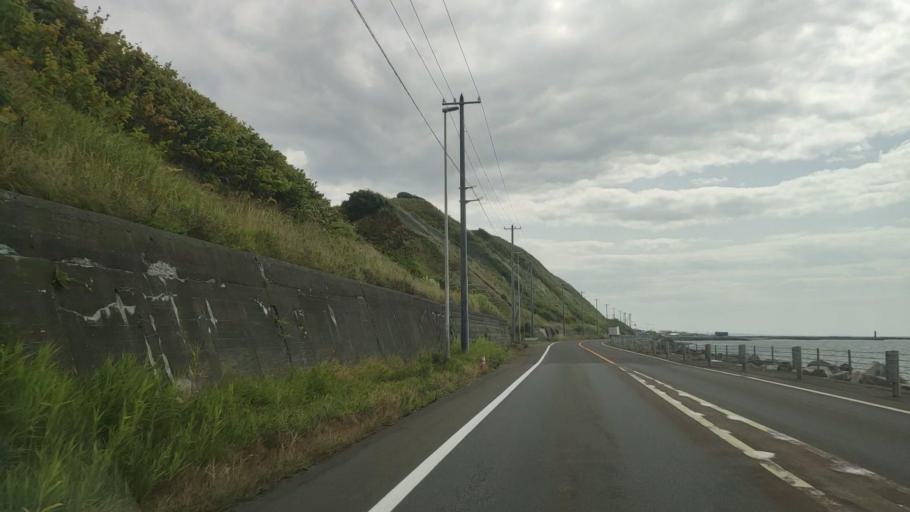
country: JP
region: Hokkaido
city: Rumoi
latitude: 44.5441
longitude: 141.7668
